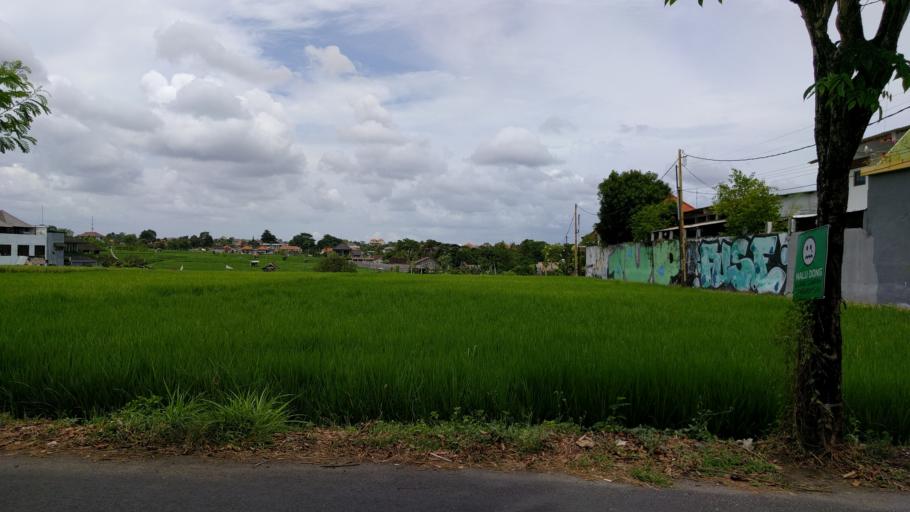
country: ID
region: Bali
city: Banjar Gunungpande
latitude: -8.6498
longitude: 115.1496
